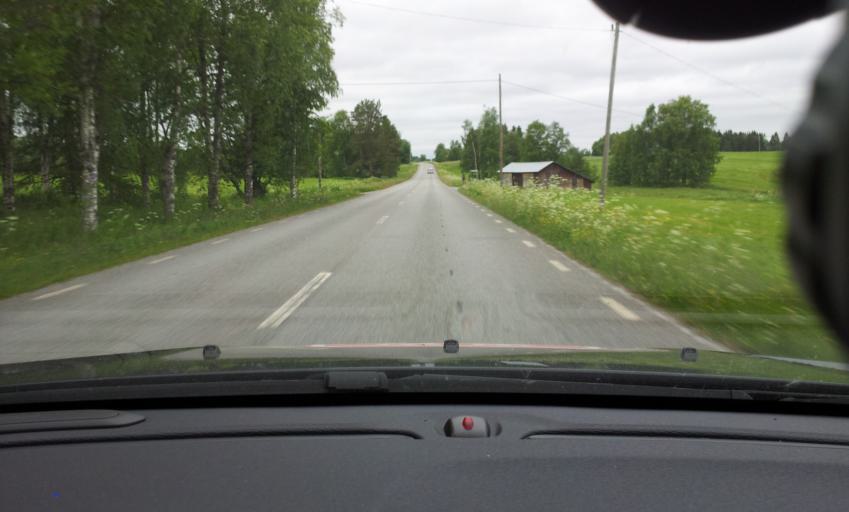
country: SE
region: Jaemtland
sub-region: Krokoms Kommun
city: Krokom
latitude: 63.1401
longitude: 14.1873
